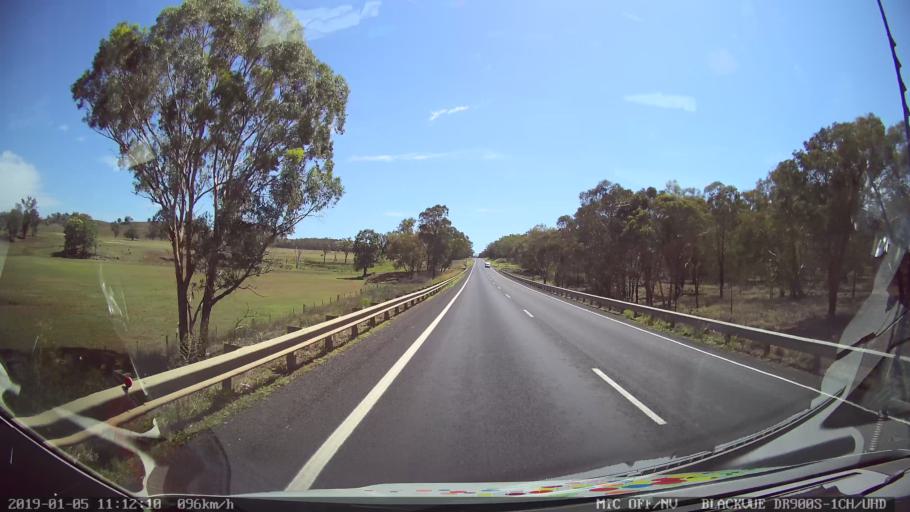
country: AU
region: New South Wales
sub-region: Warrumbungle Shire
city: Coonabarabran
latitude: -31.3848
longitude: 149.2577
